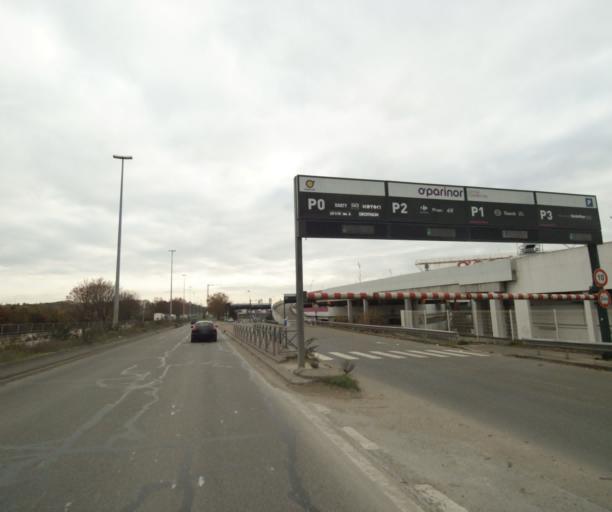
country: FR
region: Ile-de-France
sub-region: Departement de Seine-Saint-Denis
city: Le Blanc-Mesnil
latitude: 48.9597
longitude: 2.4759
